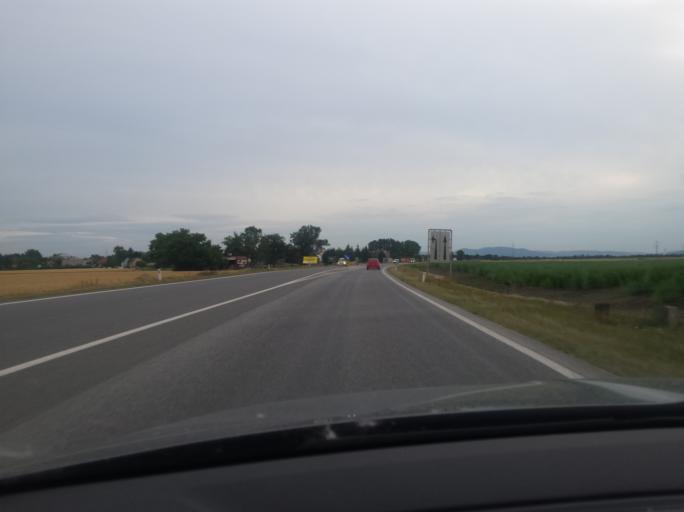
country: AT
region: Lower Austria
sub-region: Politischer Bezirk Ganserndorf
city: Aderklaa
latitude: 48.2885
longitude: 16.5451
